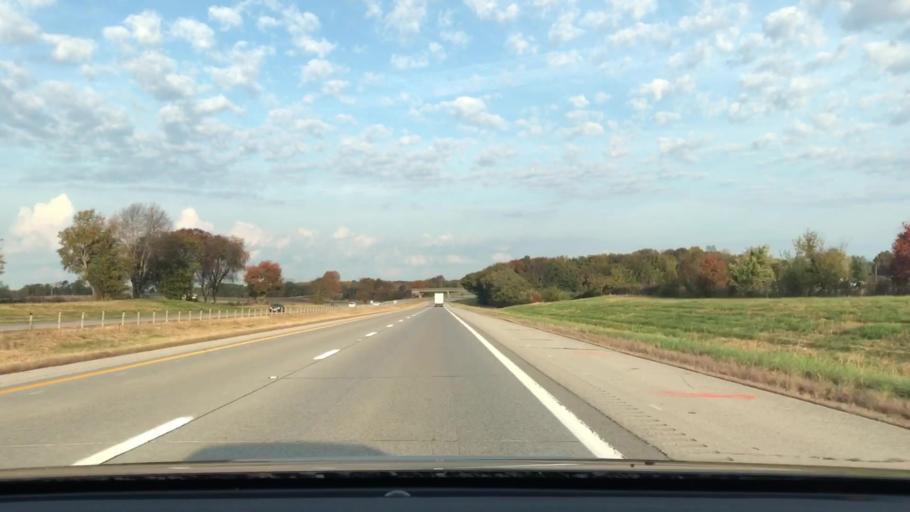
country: US
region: Kentucky
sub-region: Christian County
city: Hopkinsville
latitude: 36.8253
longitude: -87.6541
